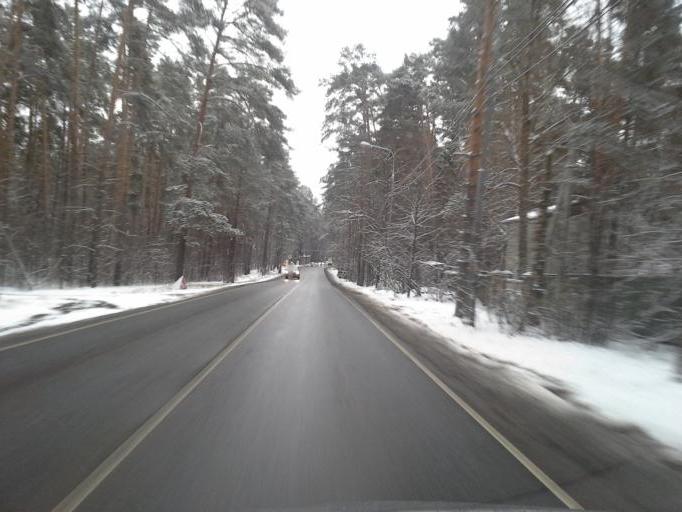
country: RU
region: Moskovskaya
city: Nikolina Gora
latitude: 55.7330
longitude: 37.0433
